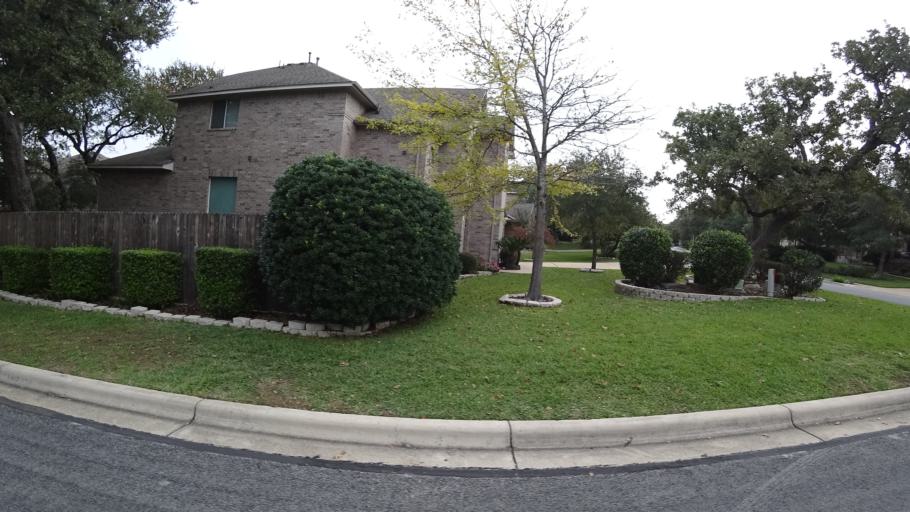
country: US
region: Texas
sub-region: Travis County
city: Shady Hollow
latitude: 30.1921
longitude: -97.8963
